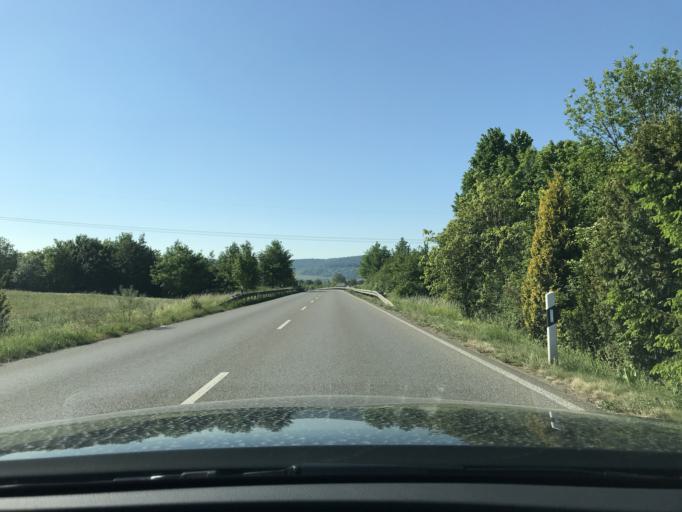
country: DE
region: Baden-Wuerttemberg
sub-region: Regierungsbezirk Stuttgart
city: Fellbach
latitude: 48.8262
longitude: 9.2898
